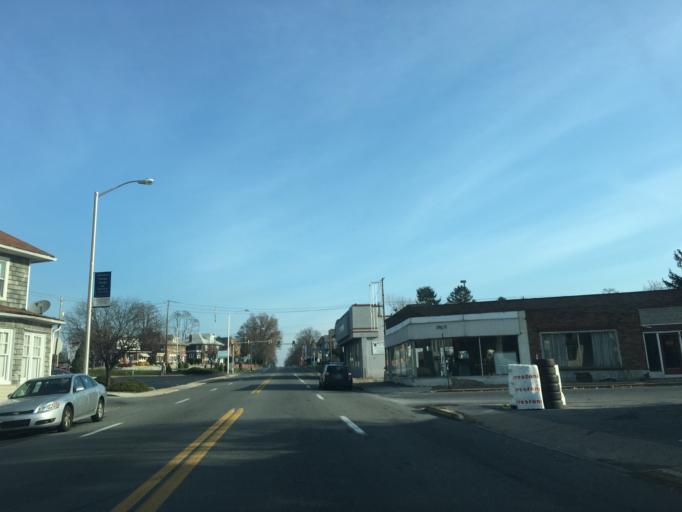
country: US
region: Pennsylvania
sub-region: Dauphin County
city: Penbrook
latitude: 40.2812
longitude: -76.8462
